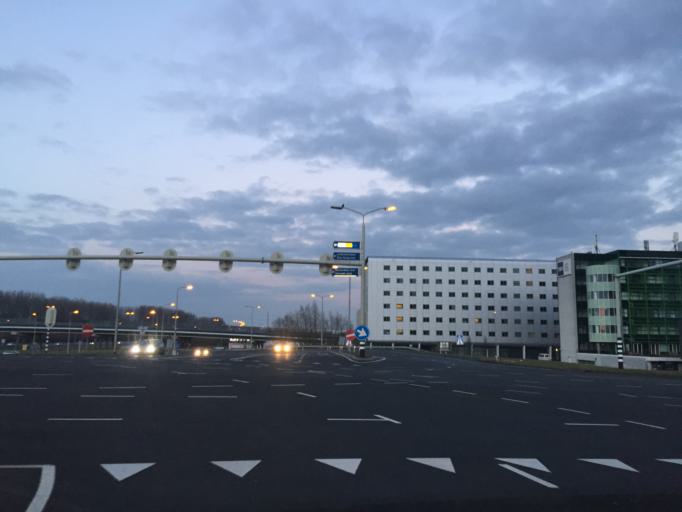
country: NL
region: South Holland
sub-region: Gemeente Leidschendam-Voorburg
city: Voorburg
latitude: 52.0723
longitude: 4.3968
